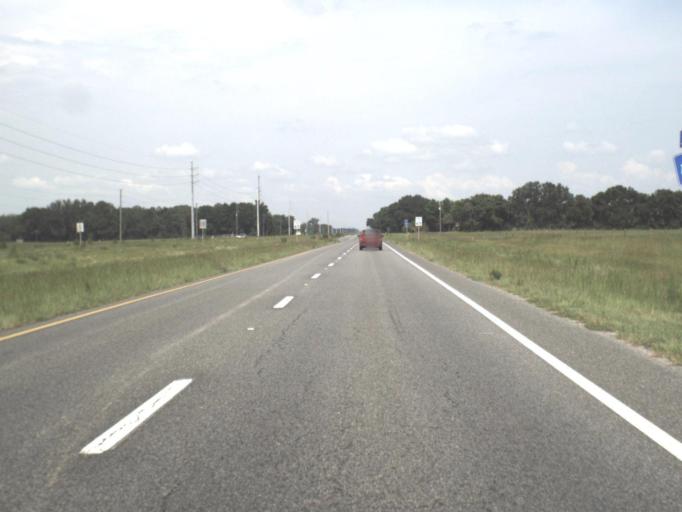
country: US
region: Florida
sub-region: Levy County
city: Chiefland
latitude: 29.4752
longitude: -82.7523
